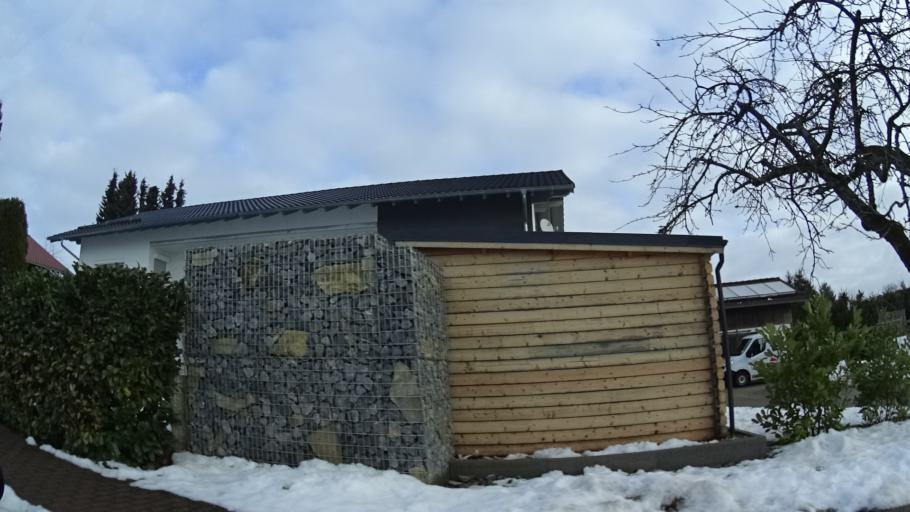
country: DE
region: Baden-Wuerttemberg
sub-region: Karlsruhe Region
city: Limbach
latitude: 49.4818
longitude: 9.1707
